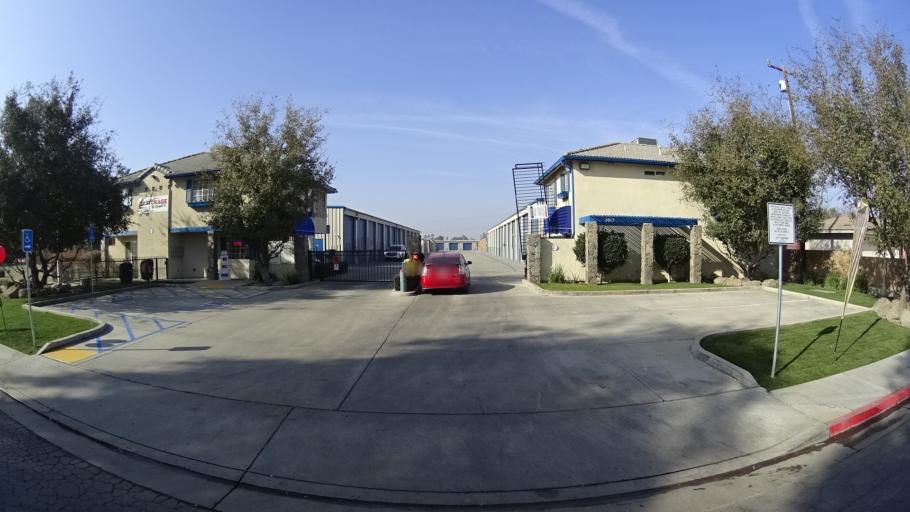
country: US
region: California
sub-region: Kern County
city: Bakersfield
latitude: 35.3194
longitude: -119.0345
